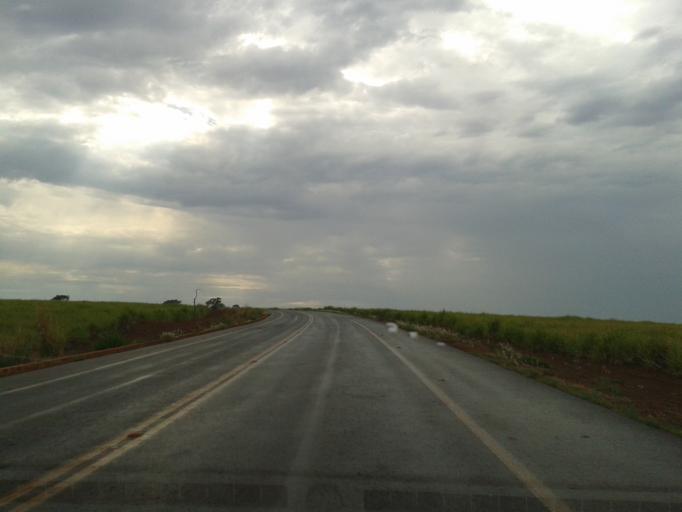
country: BR
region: Minas Gerais
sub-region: Centralina
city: Centralina
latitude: -18.6907
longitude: -49.3638
